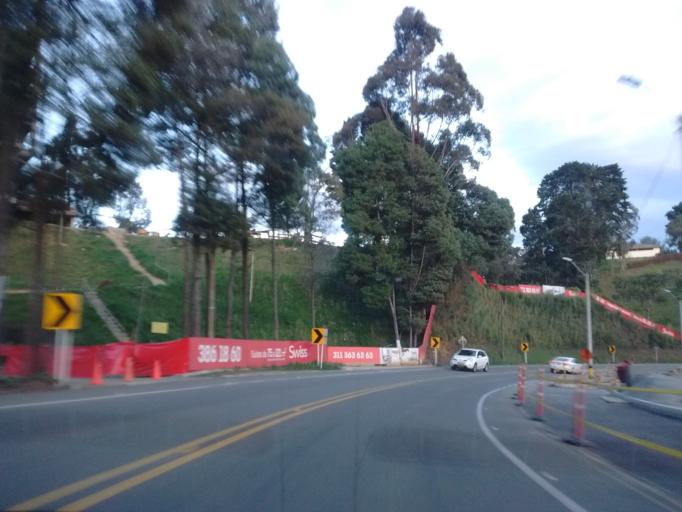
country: CO
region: Antioquia
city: Envigado
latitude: 6.1557
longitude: -75.5316
